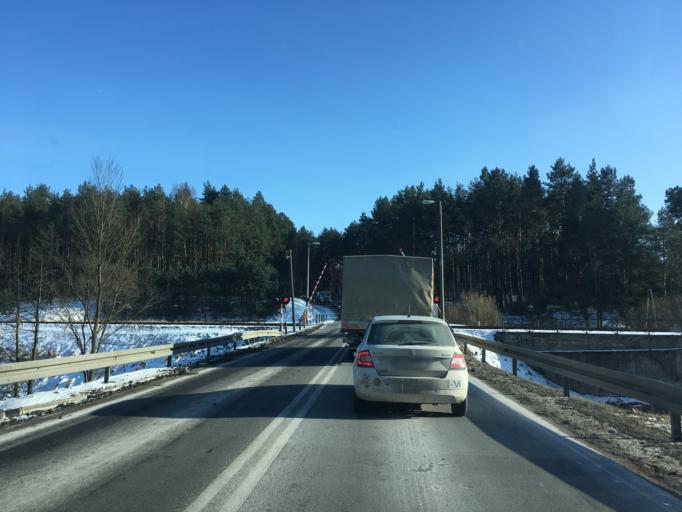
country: PL
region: Pomeranian Voivodeship
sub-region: Powiat koscierski
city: Koscierzyna
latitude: 54.1184
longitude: 17.8890
